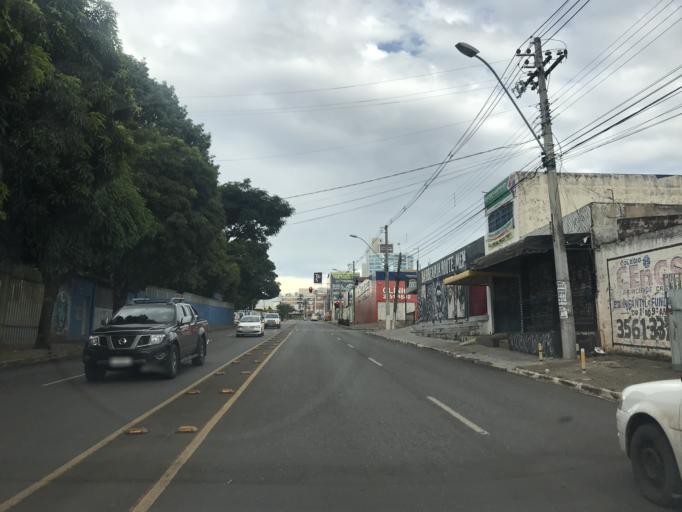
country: BR
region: Federal District
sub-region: Brasilia
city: Brasilia
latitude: -15.8433
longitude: -48.0486
